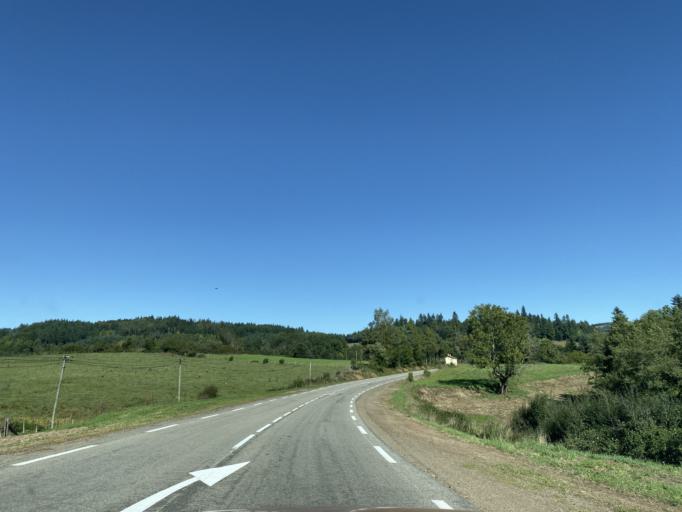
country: FR
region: Rhone-Alpes
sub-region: Departement de la Loire
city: Saint-Just-en-Chevalet
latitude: 45.8894
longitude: 3.8434
